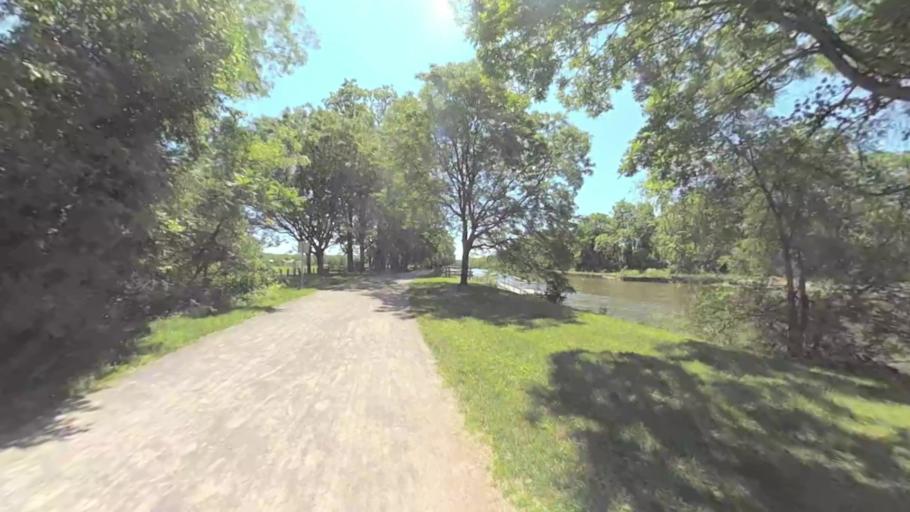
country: US
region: New York
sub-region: Monroe County
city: Pittsford
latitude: 43.0743
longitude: -77.4933
